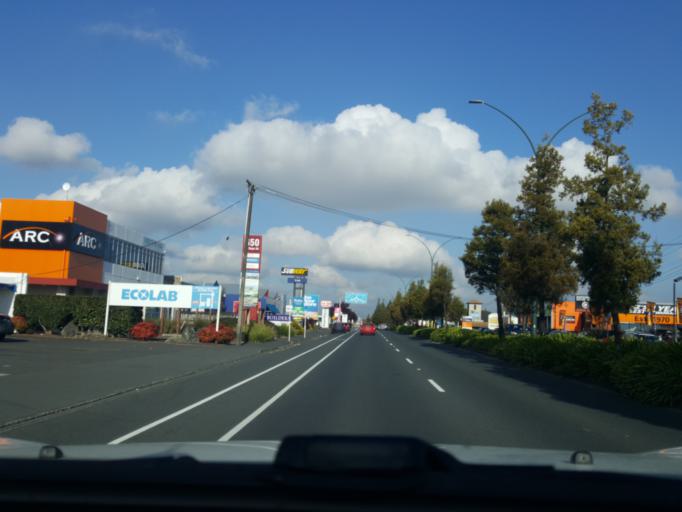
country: NZ
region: Waikato
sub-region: Hamilton City
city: Hamilton
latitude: -37.7556
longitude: 175.2440
